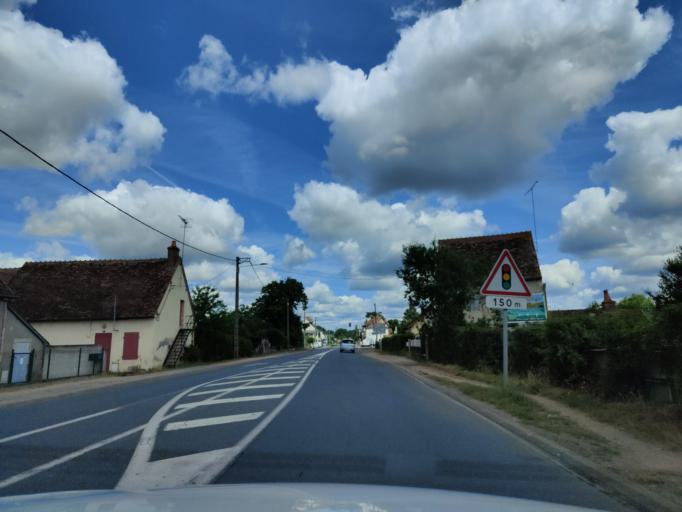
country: FR
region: Auvergne
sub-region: Departement de l'Allier
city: Vallon-en-Sully
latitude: 46.5314
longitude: 2.6214
